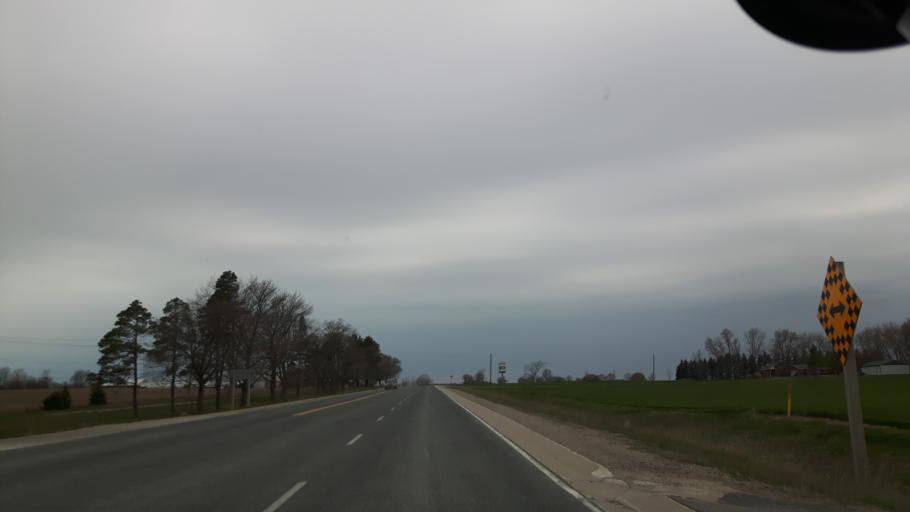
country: CA
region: Ontario
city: Goderich
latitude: 43.6512
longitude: -81.6089
